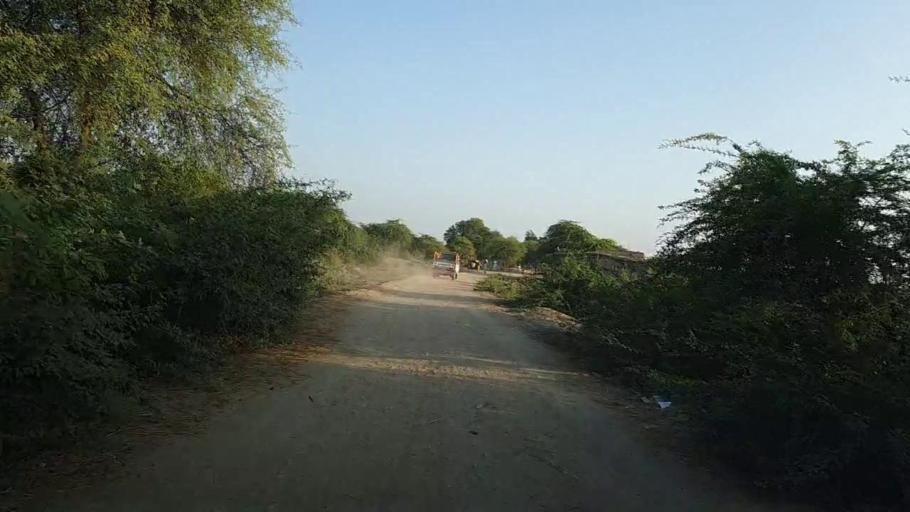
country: PK
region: Sindh
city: Kario
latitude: 24.6925
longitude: 68.6723
